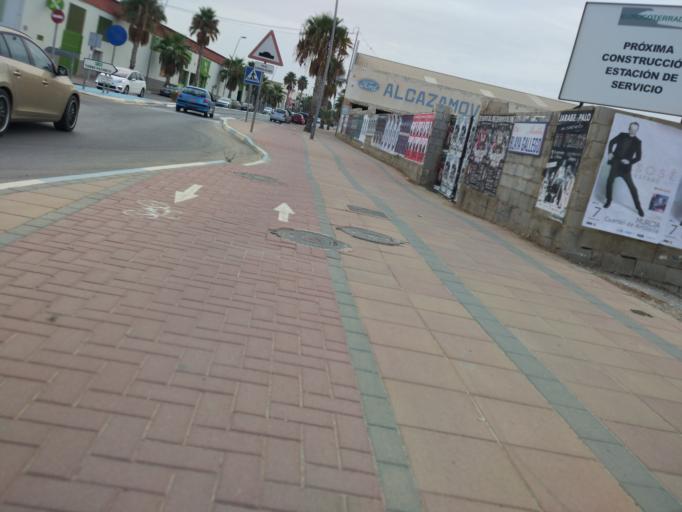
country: ES
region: Murcia
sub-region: Murcia
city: Los Alcazares
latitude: 37.7385
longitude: -0.8624
